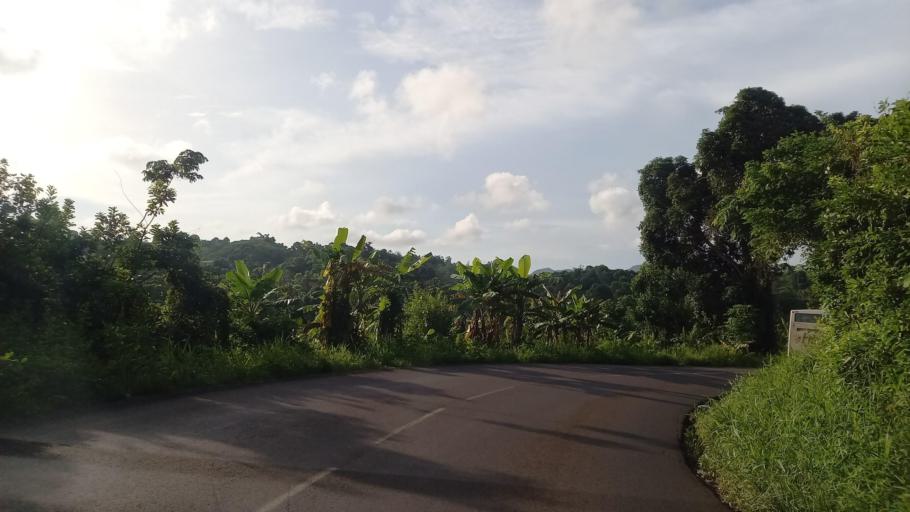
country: YT
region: Bandraboua
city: Bandraboua
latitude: -12.7387
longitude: 45.1181
